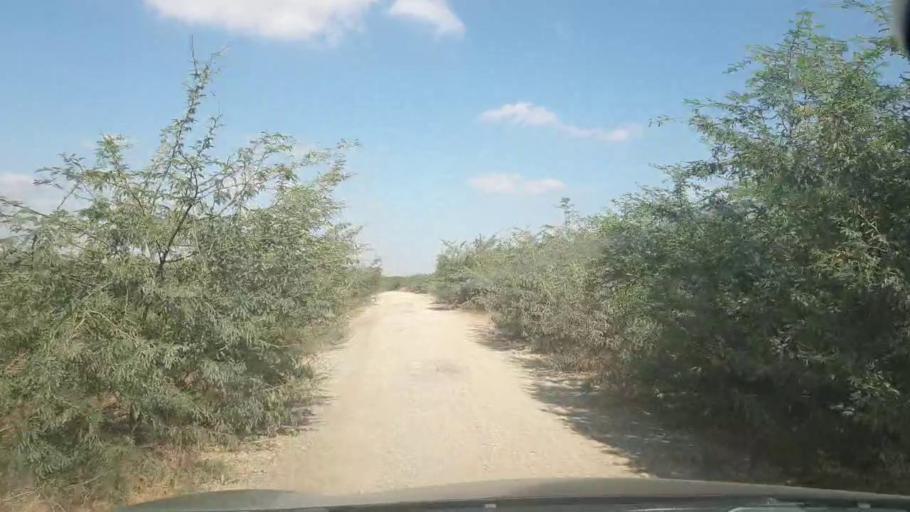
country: PK
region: Sindh
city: Malir Cantonment
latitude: 25.0636
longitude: 67.3954
